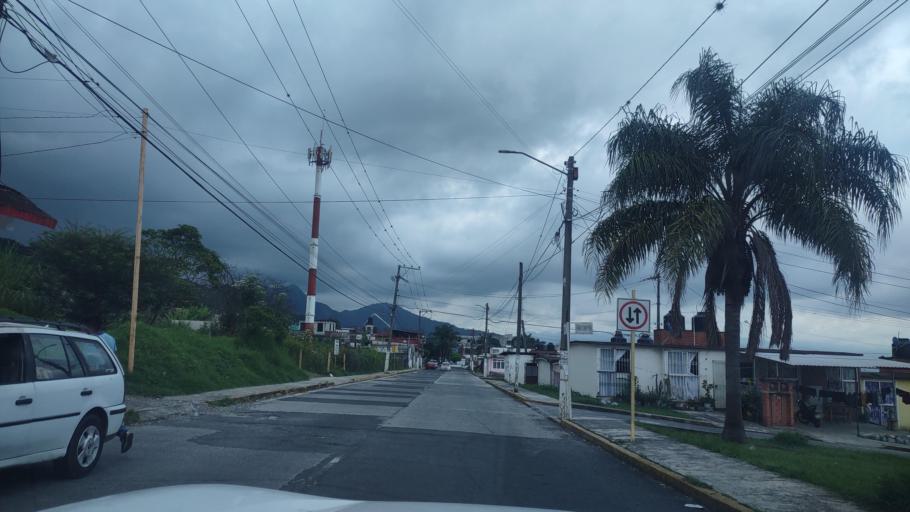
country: MX
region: Veracruz
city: Ixtac Zoquitlan
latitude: 18.8832
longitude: -97.0656
